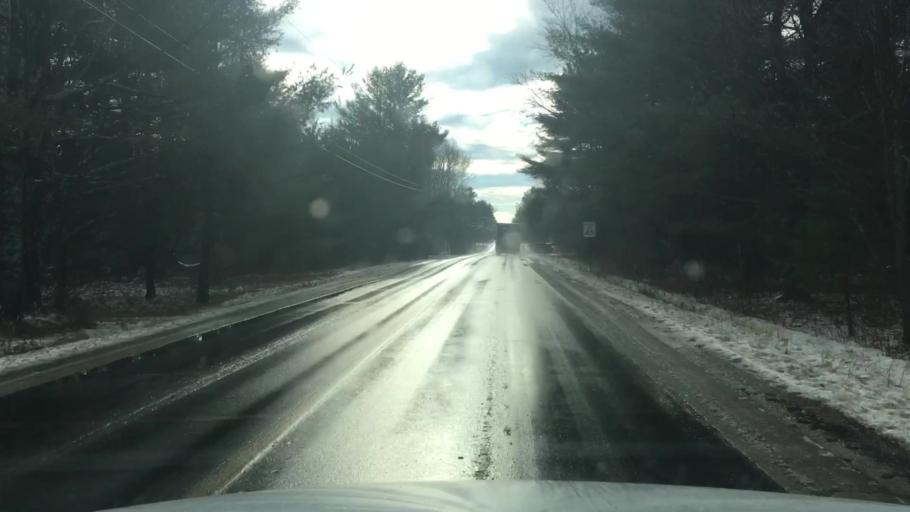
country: US
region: Maine
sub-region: Penobscot County
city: Brewer
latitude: 44.7497
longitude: -68.7675
